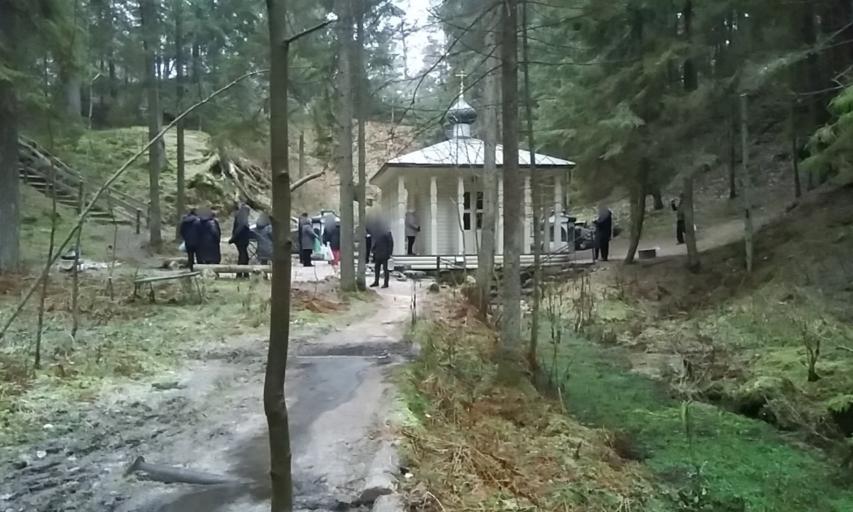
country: RU
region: Leningrad
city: Luga
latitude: 58.7601
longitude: 29.9272
